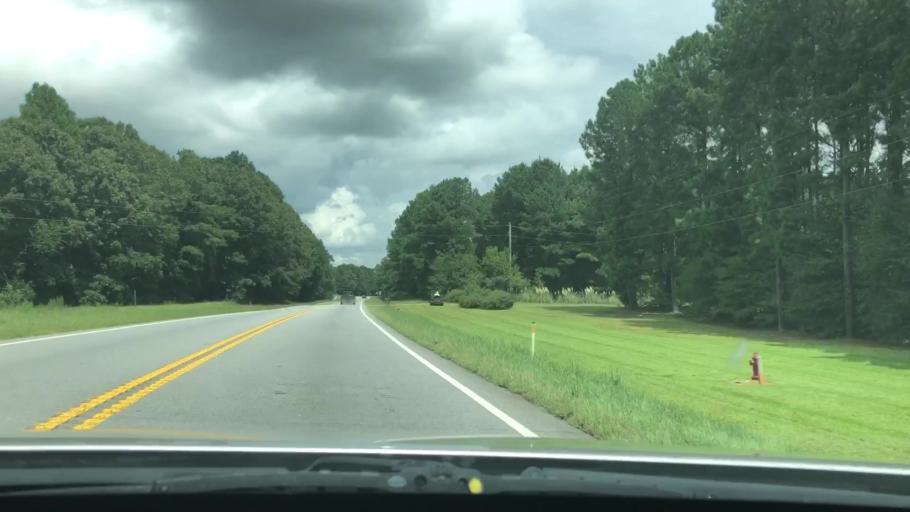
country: US
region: Georgia
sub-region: Lamar County
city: Barnesville
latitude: 33.1604
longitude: -84.1096
